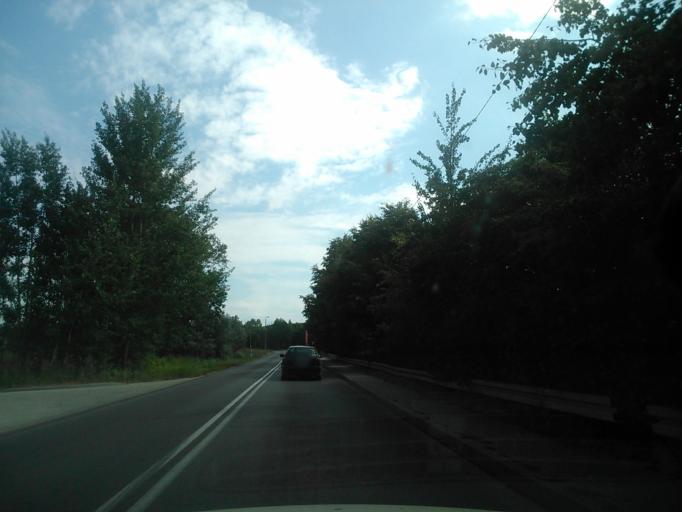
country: PL
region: Warmian-Masurian Voivodeship
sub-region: Powiat dzialdowski
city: Ilowo -Osada
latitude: 53.1623
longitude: 20.2981
